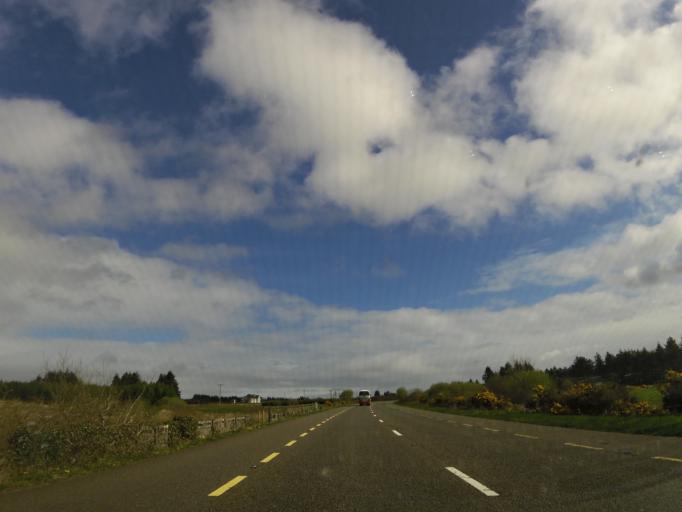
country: IE
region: Connaught
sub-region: Maigh Eo
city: Ballyhaunis
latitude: 53.9000
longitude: -8.7988
